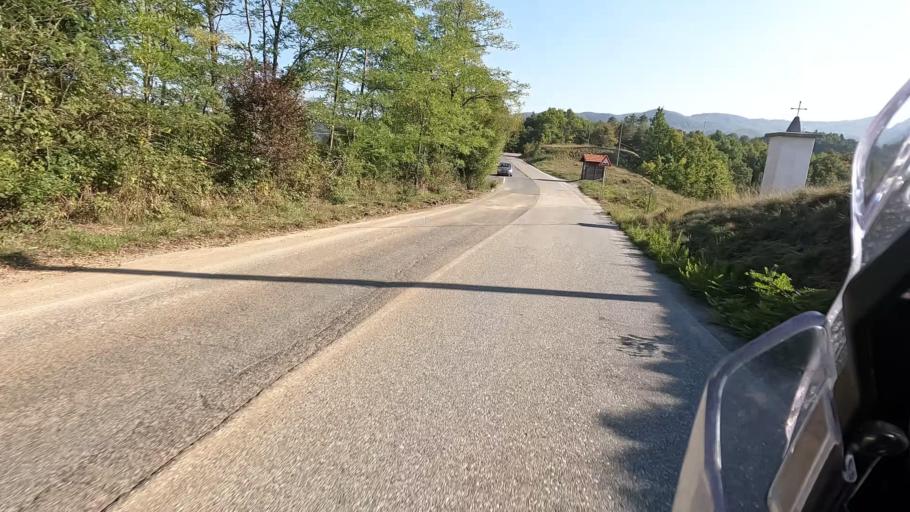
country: IT
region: Liguria
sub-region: Provincia di Savona
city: Urbe
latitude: 44.5010
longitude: 8.5446
